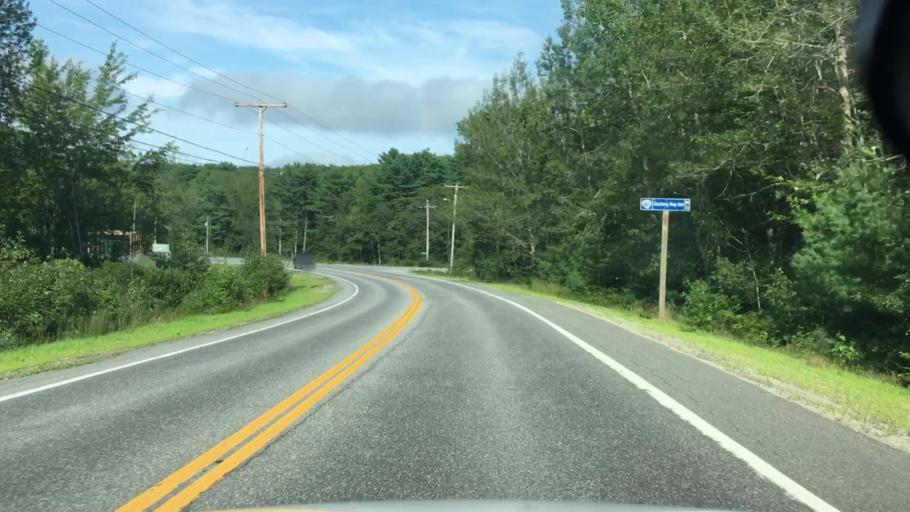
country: US
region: Maine
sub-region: Cumberland County
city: Harpswell Center
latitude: 43.8138
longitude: -69.9253
